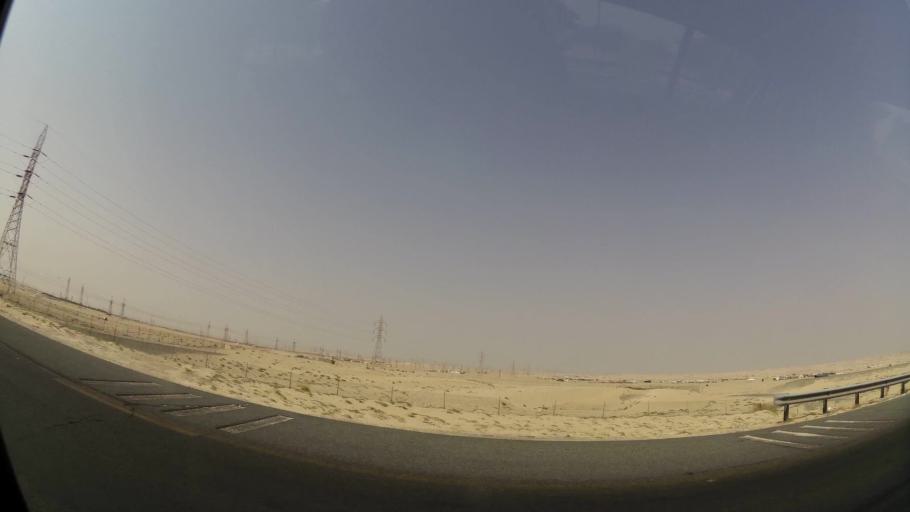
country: KW
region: Muhafazat al Jahra'
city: Al Jahra'
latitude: 29.3488
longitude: 47.6307
